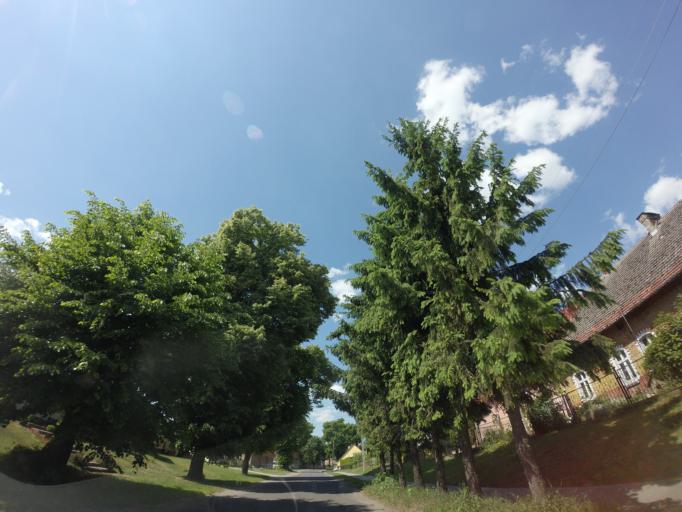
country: PL
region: West Pomeranian Voivodeship
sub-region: Powiat choszczenski
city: Pelczyce
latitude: 53.1140
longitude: 15.2538
